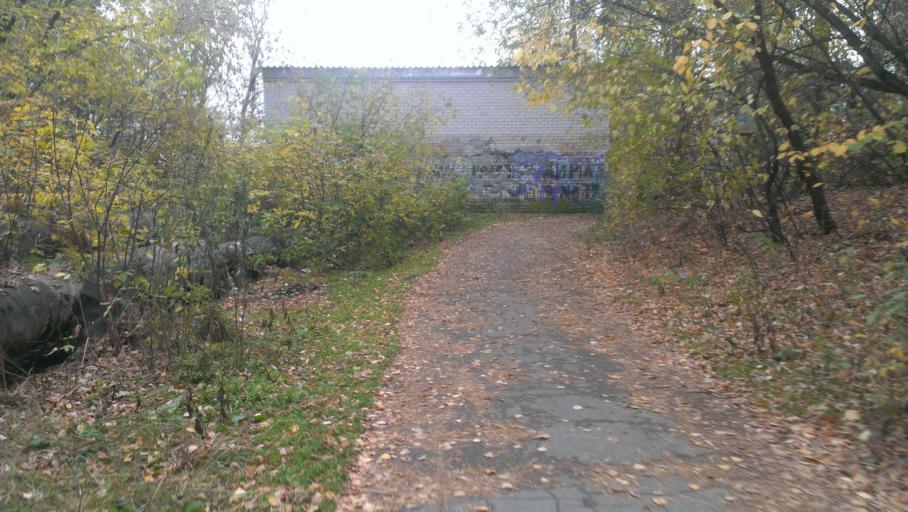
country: RU
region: Altai Krai
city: Yuzhnyy
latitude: 53.2584
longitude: 83.6899
